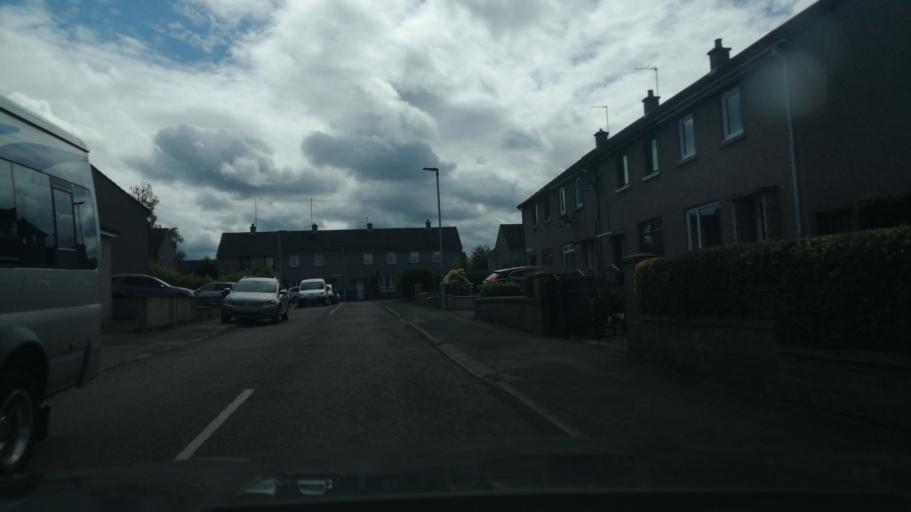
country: GB
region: Scotland
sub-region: Moray
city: Elgin
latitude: 57.6568
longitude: -3.3090
